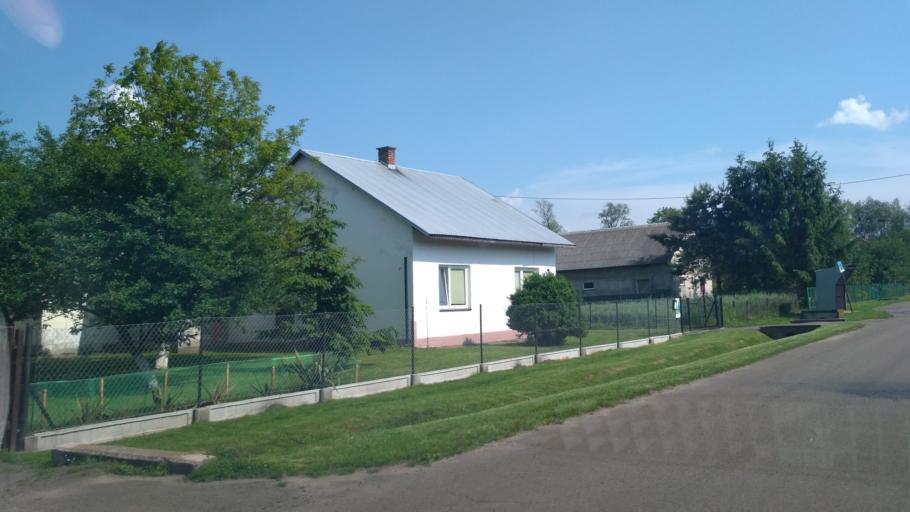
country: PL
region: Subcarpathian Voivodeship
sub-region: Powiat jaroslawski
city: Ostrow
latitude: 49.9382
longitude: 22.7540
